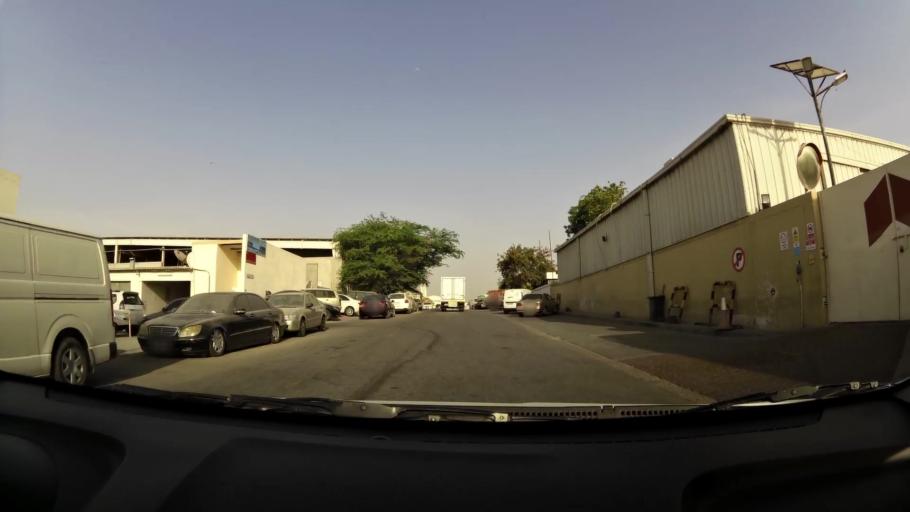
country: AE
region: Ash Shariqah
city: Sharjah
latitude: 25.2264
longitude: 55.3633
